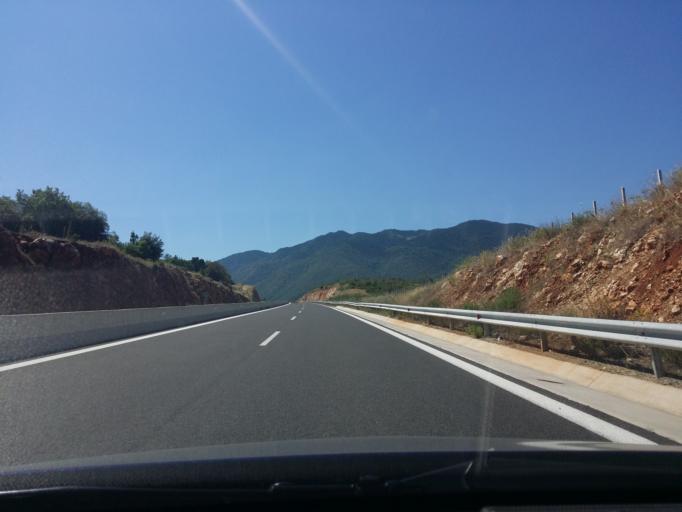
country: GR
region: Peloponnese
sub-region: Nomos Arkadias
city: Megalopoli
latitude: 37.2945
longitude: 22.2115
